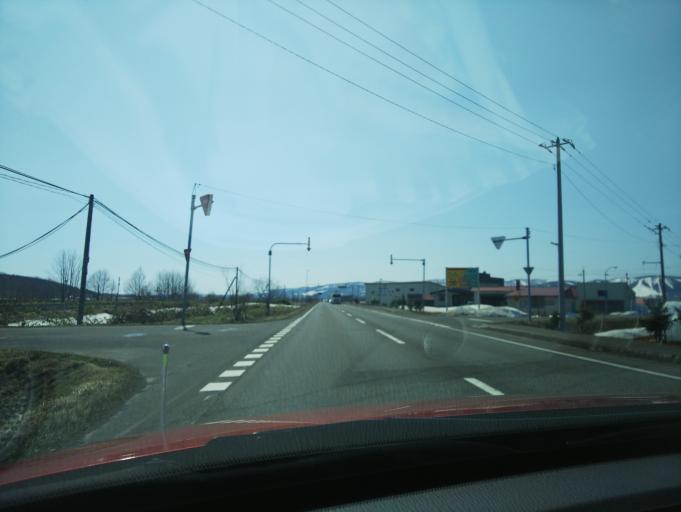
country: JP
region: Hokkaido
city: Nayoro
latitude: 44.2762
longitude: 142.4025
